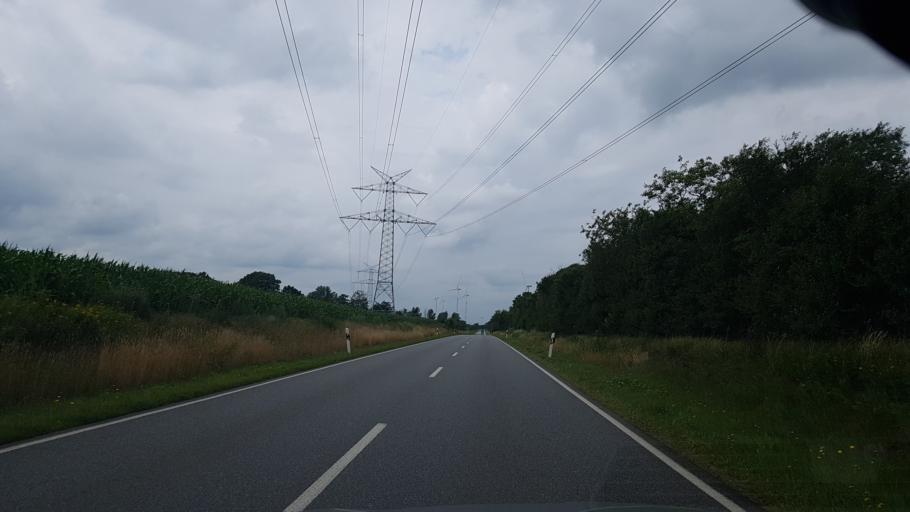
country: DE
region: Schleswig-Holstein
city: Jardelund
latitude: 54.8310
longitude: 9.2163
